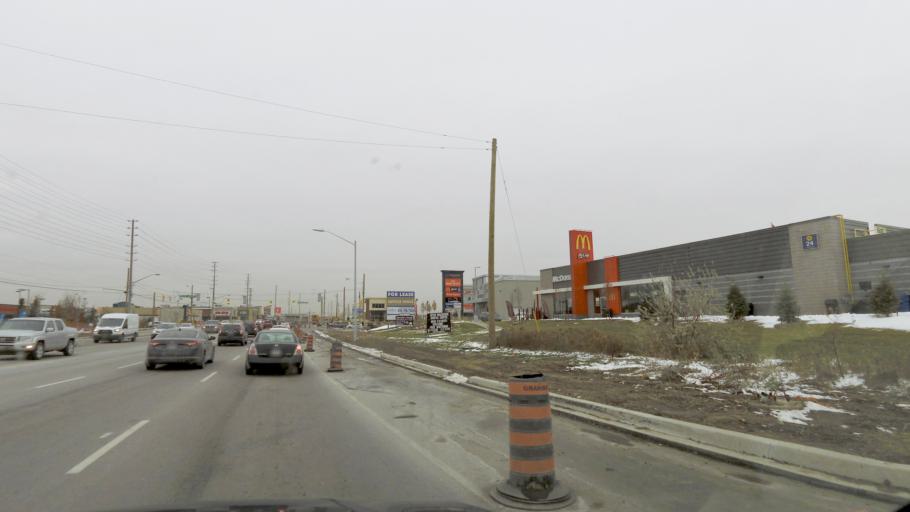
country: CA
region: Ontario
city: Vaughan
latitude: 43.8460
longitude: -79.5526
